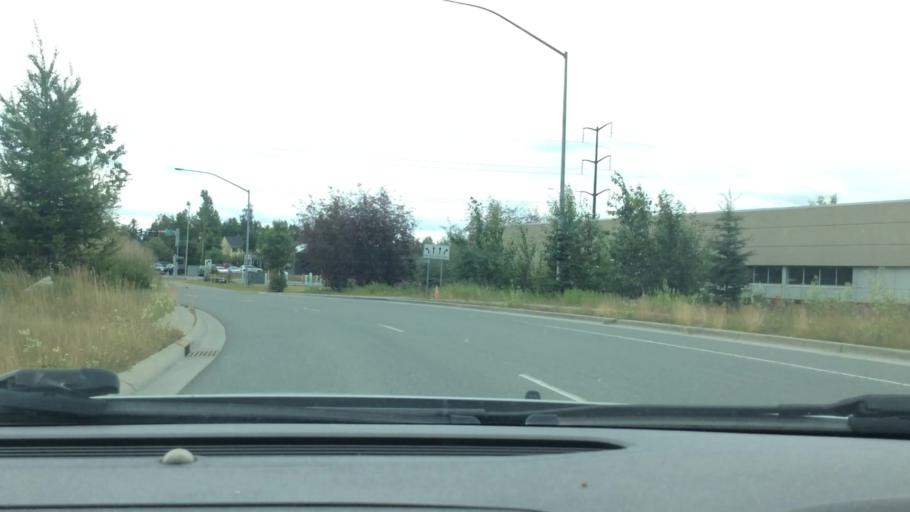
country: US
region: Alaska
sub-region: Anchorage Municipality
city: Anchorage
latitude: 61.1795
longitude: -149.7785
